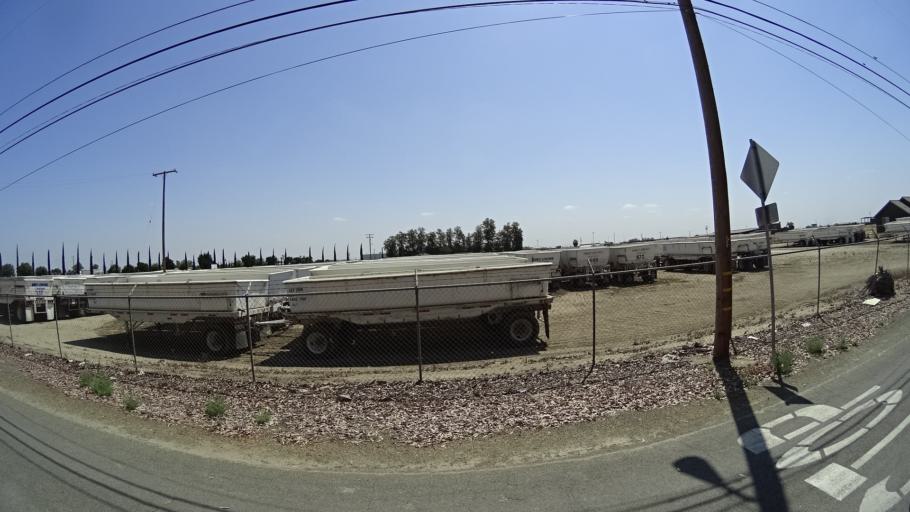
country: US
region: California
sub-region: Kings County
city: Home Garden
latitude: 36.3222
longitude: -119.6212
